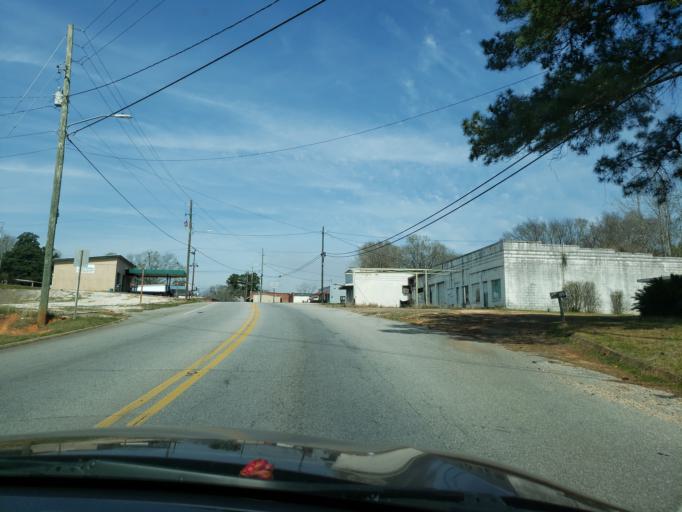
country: US
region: Alabama
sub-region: Elmore County
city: Tallassee
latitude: 32.5431
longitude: -85.8738
